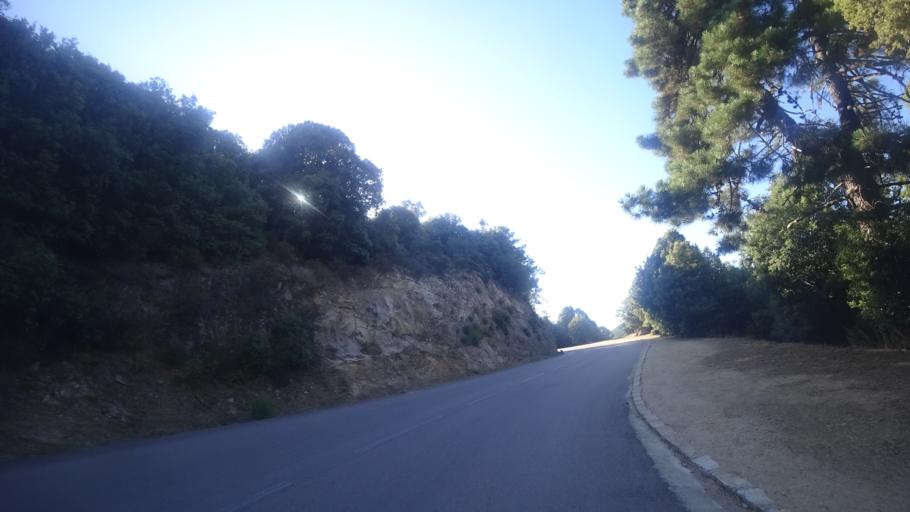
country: FR
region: Corsica
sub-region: Departement de la Corse-du-Sud
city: Cargese
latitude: 42.2390
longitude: 8.6523
